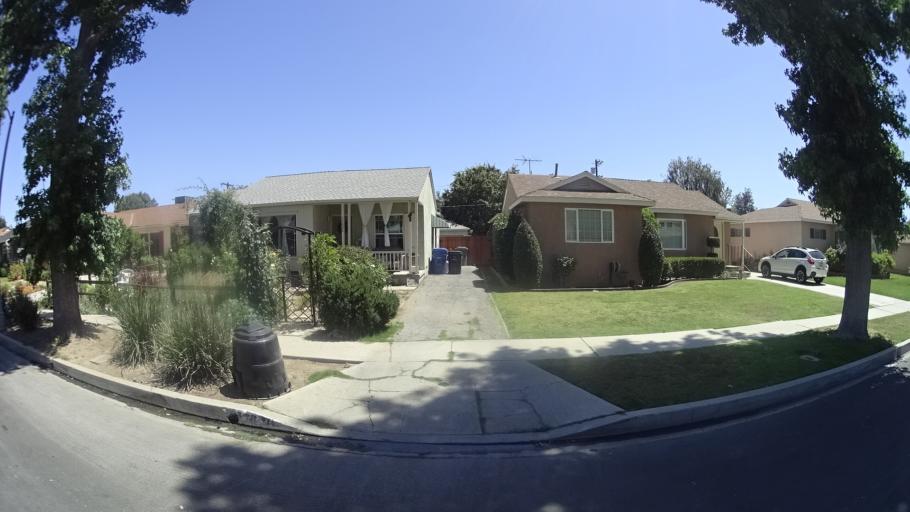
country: US
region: California
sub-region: Los Angeles County
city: Northridge
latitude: 34.1902
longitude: -118.5174
